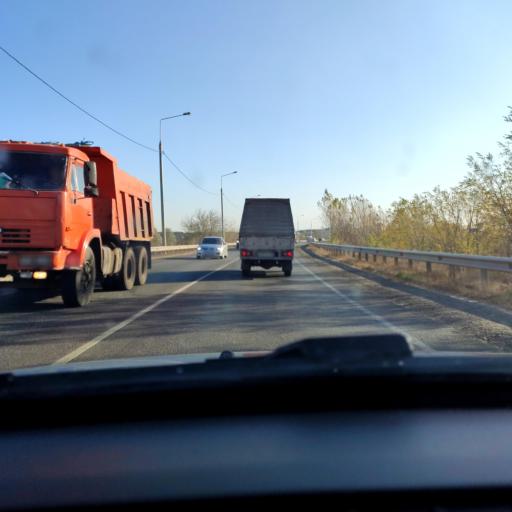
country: RU
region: Voronezj
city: Pridonskoy
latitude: 51.7174
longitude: 39.0739
